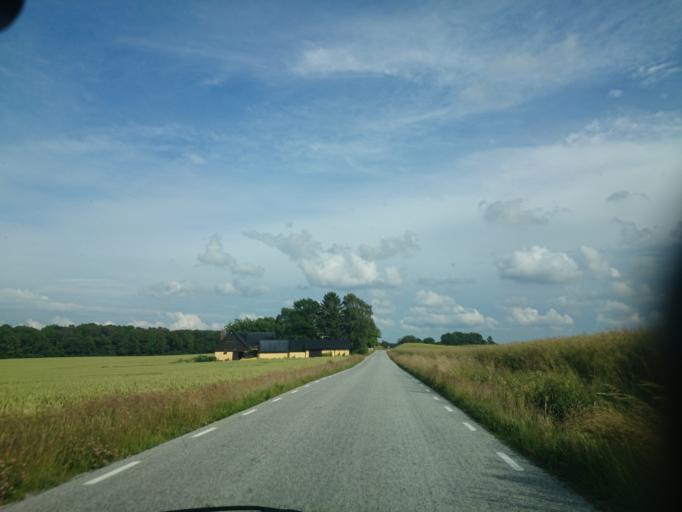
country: SE
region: Skane
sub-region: Lunds Kommun
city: Lund
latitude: 55.7342
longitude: 13.2917
